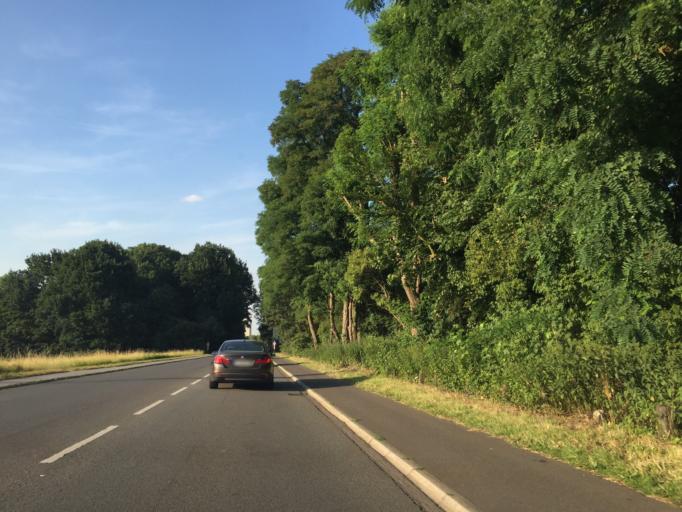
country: DE
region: North Rhine-Westphalia
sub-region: Regierungsbezirk Koln
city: Neustadt/Sued
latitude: 50.9015
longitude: 6.9127
